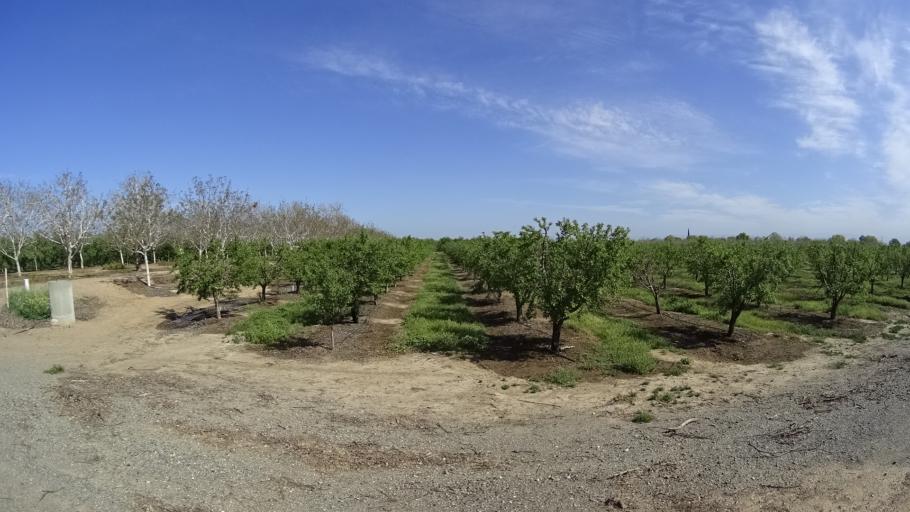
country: US
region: California
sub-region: Glenn County
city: Hamilton City
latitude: 39.6668
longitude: -122.0130
